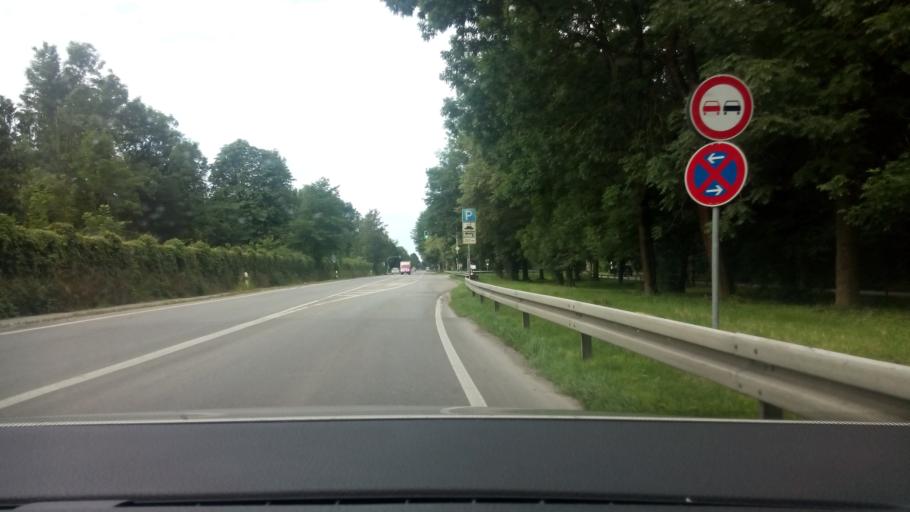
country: DE
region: Bavaria
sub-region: Upper Bavaria
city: Unterfoehring
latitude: 48.2125
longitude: 11.6347
